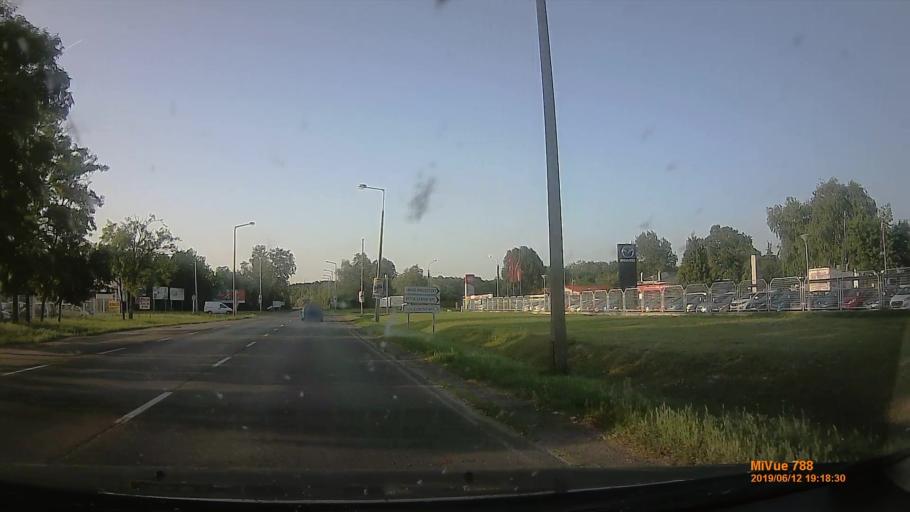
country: HU
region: Bacs-Kiskun
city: Kecskemet
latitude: 46.8905
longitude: 19.7050
